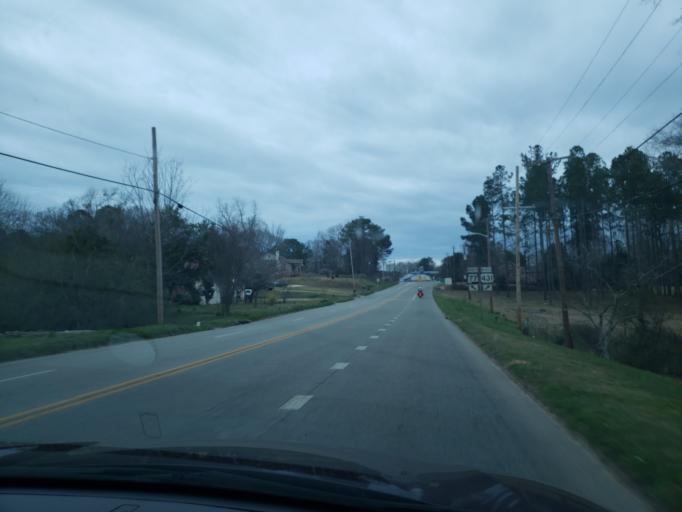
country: US
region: Alabama
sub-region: Chambers County
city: Lafayette
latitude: 32.9081
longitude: -85.4013
